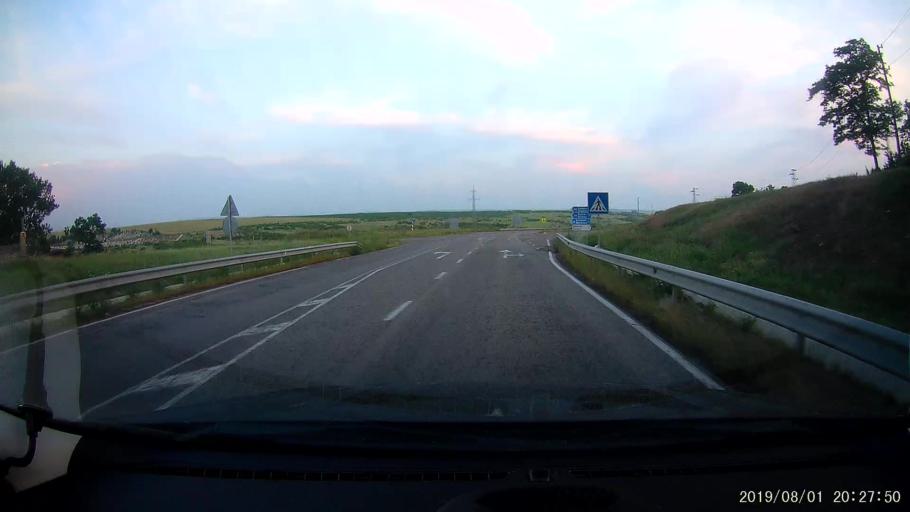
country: BG
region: Yambol
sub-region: Obshtina Elkhovo
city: Elkhovo
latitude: 42.1744
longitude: 26.5834
